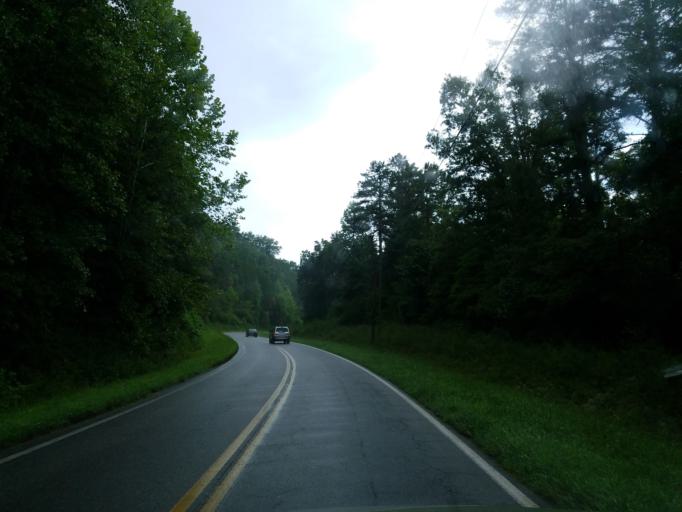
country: US
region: Georgia
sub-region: Lumpkin County
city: Dahlonega
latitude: 34.5452
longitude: -83.8857
